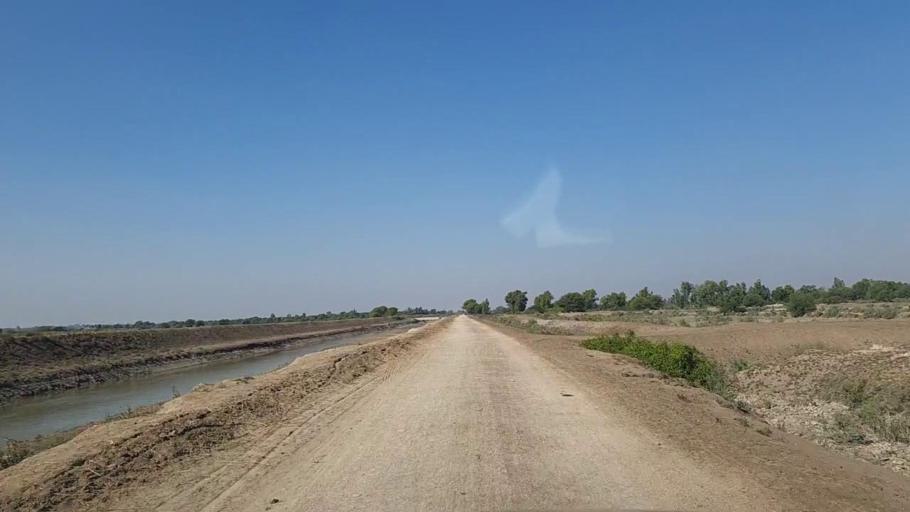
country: PK
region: Sindh
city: Mirpur Batoro
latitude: 24.7230
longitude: 68.2331
